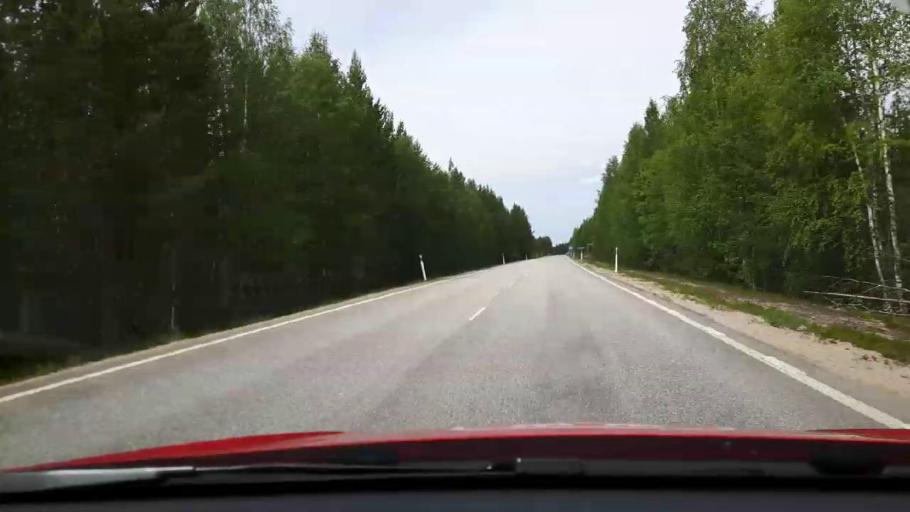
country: SE
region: Jaemtland
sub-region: Harjedalens Kommun
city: Sveg
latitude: 62.1143
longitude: 14.1790
